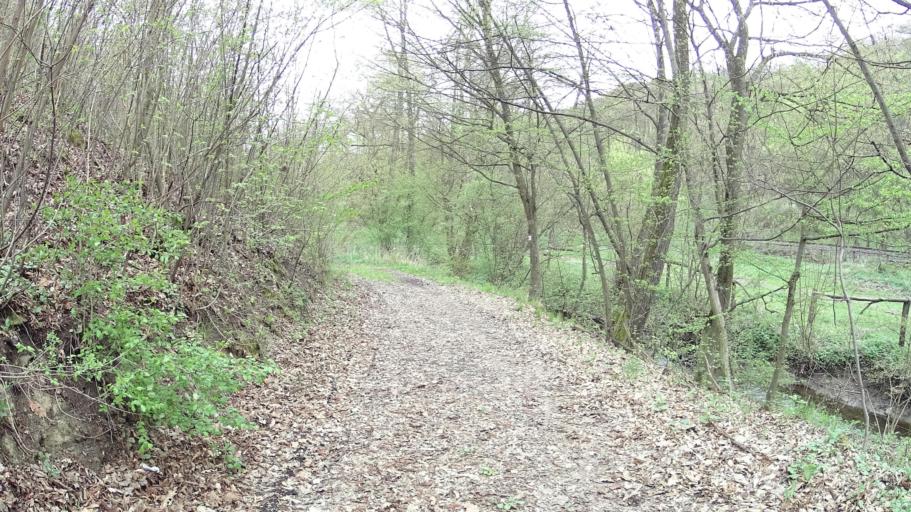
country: HU
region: Nograd
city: Diosjeno
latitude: 47.8857
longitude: 19.0422
